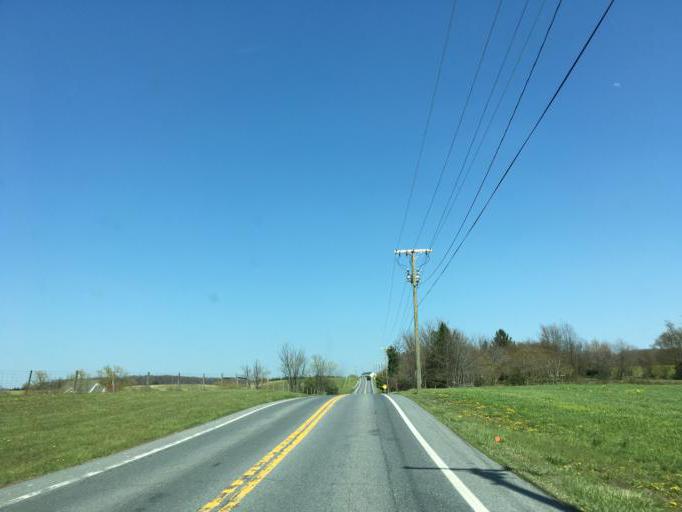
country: US
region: Maryland
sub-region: Carroll County
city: New Windsor
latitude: 39.4929
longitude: -77.1512
